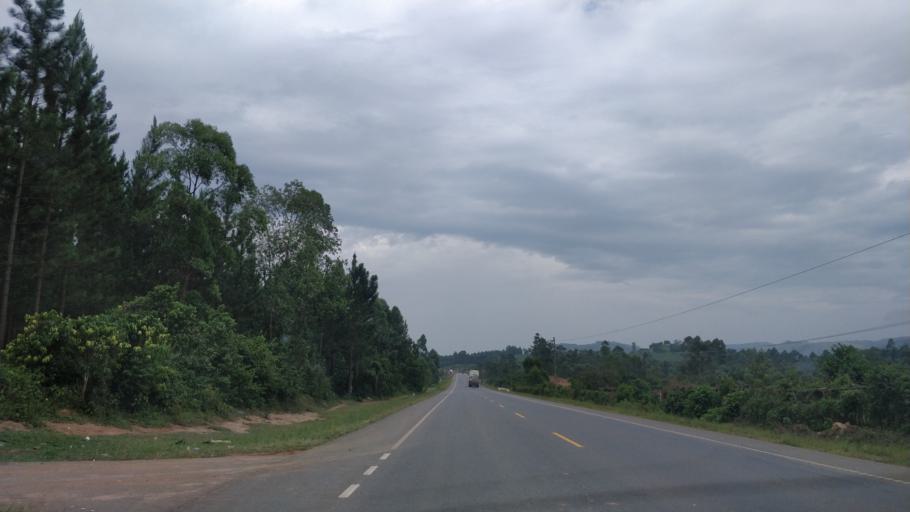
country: UG
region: Western Region
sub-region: Sheema District
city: Kibingo
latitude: -0.6698
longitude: 30.4379
